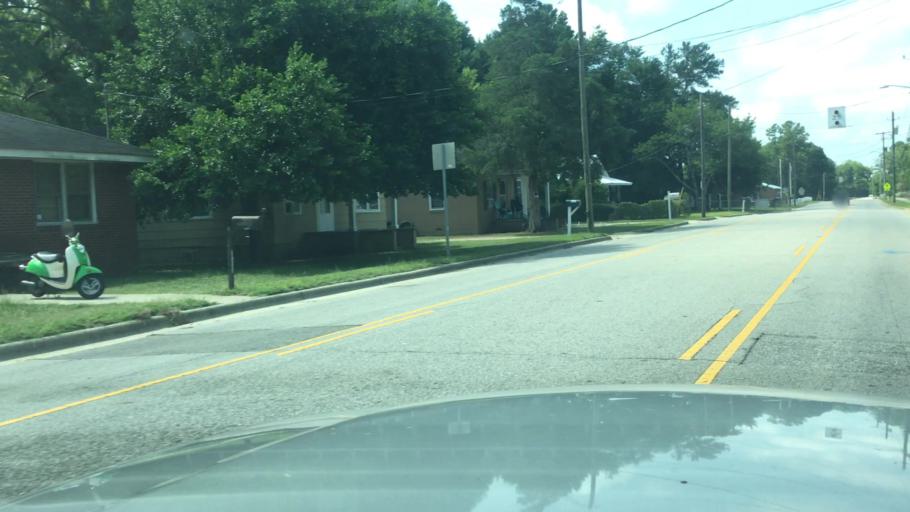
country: US
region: North Carolina
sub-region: Cumberland County
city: Fayetteville
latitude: 35.0304
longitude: -78.8968
